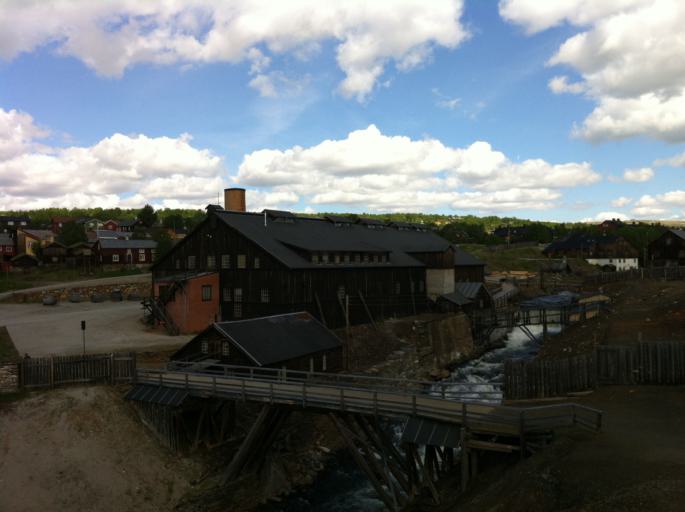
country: NO
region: Sor-Trondelag
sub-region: Roros
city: Roros
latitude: 62.5761
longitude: 11.3914
